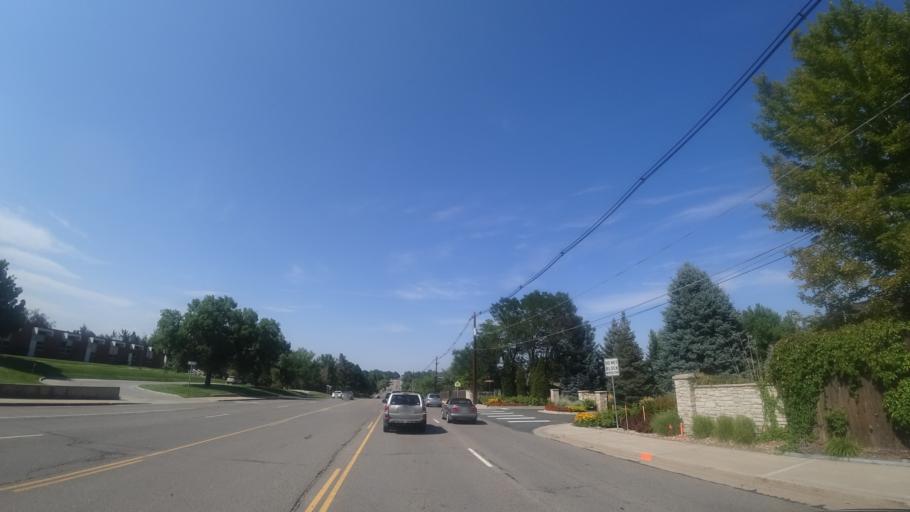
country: US
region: Colorado
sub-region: Arapahoe County
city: Cherry Hills Village
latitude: 39.6342
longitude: -104.9596
